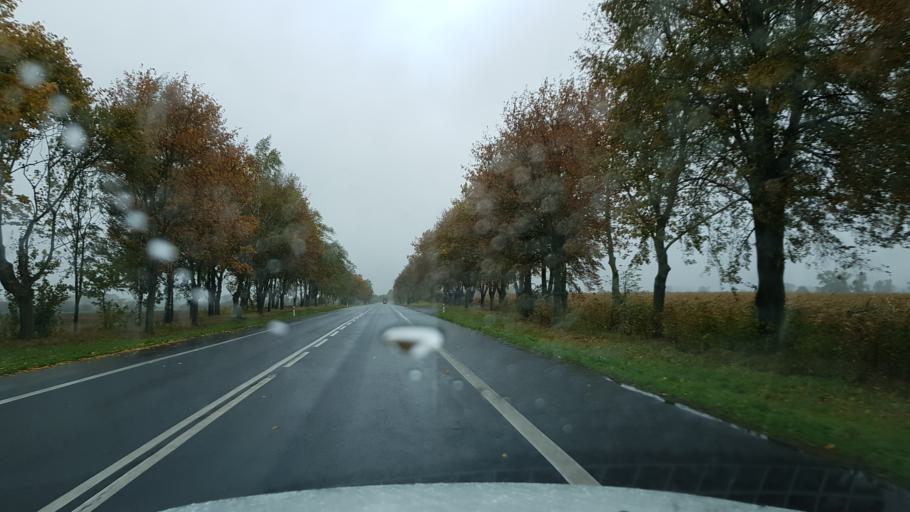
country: PL
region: West Pomeranian Voivodeship
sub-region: Powiat gryfinski
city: Stare Czarnowo
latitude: 53.2113
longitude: 14.8060
